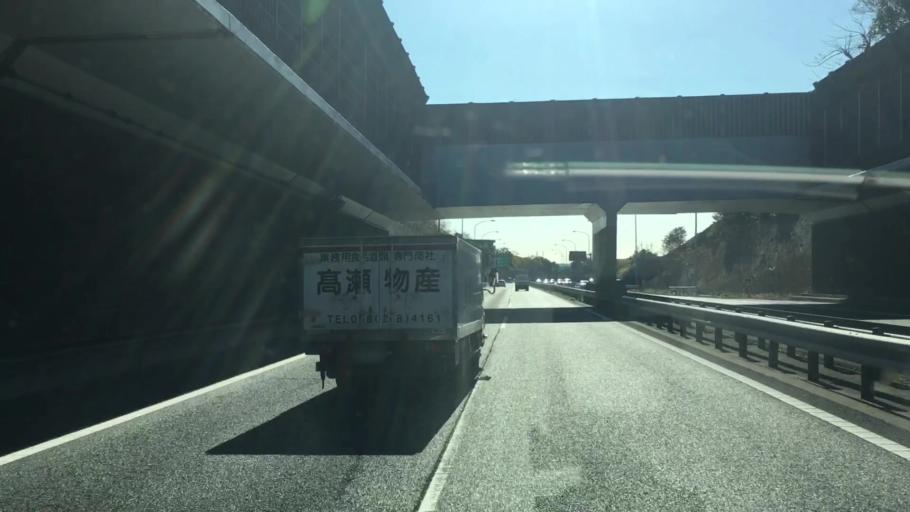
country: JP
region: Kanagawa
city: Yokohama
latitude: 35.4329
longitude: 139.5813
